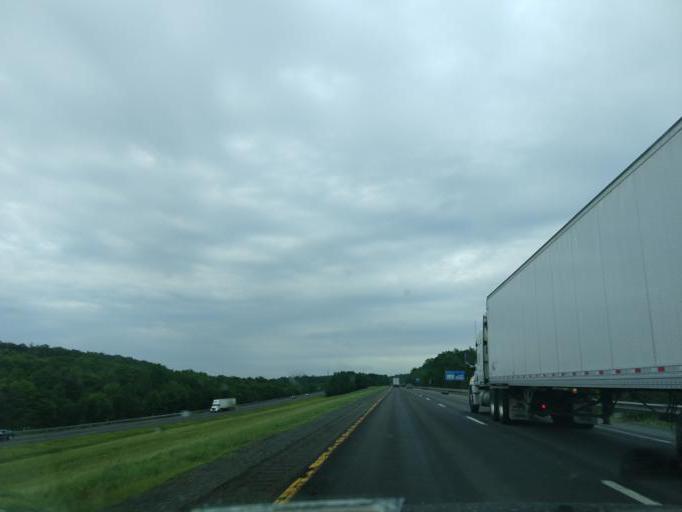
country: US
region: Pennsylvania
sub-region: Luzerne County
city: West Hazleton
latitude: 40.9607
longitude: -76.0280
